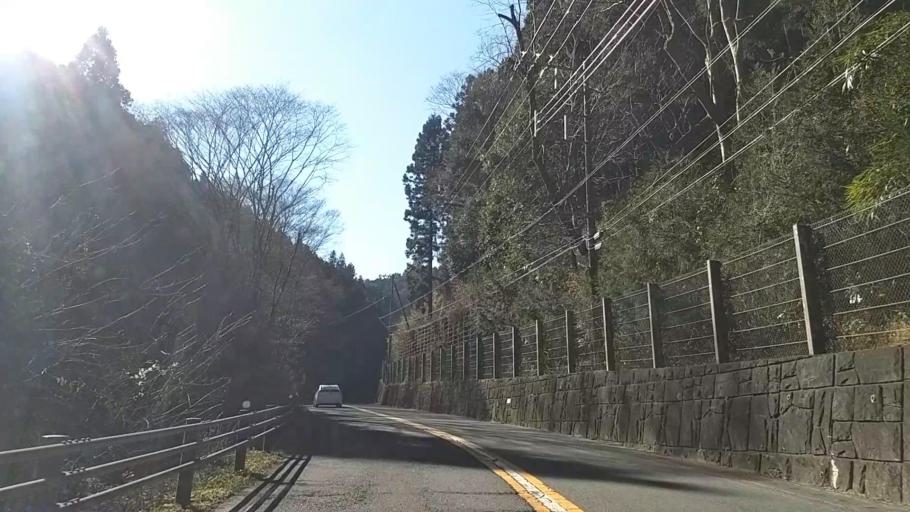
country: JP
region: Tokyo
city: Hachioji
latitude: 35.6183
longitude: 139.2528
